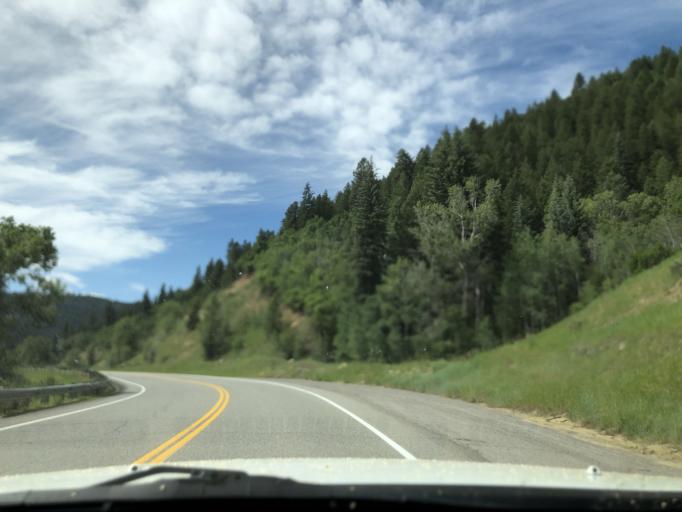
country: US
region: Colorado
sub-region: Delta County
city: Paonia
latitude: 38.9702
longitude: -107.3407
